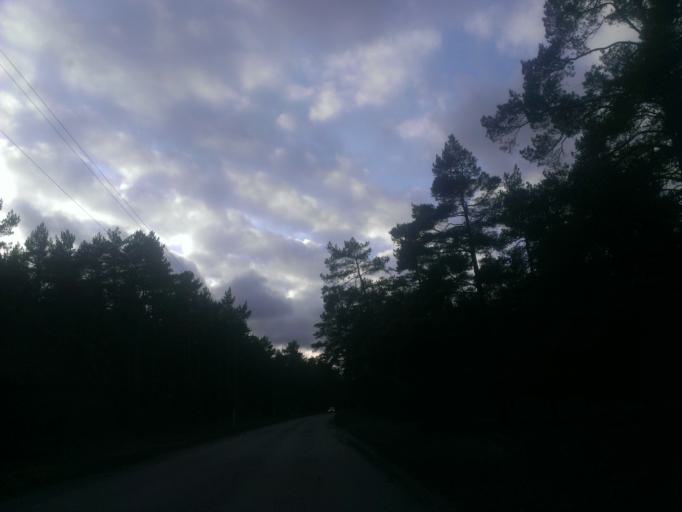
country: LV
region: Riga
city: Bolderaja
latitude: 57.0607
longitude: 24.0786
